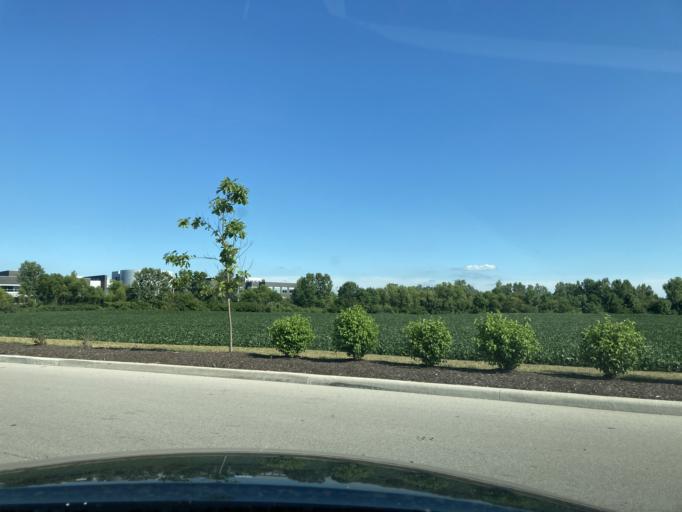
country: US
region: Indiana
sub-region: Hamilton County
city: Fishers
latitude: 39.9522
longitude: -86.0061
